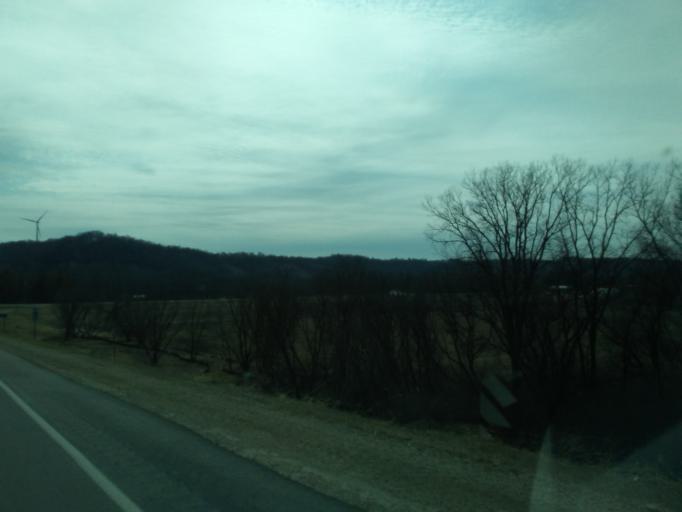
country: US
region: Iowa
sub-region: Winneshiek County
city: Decorah
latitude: 43.3241
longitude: -91.8135
